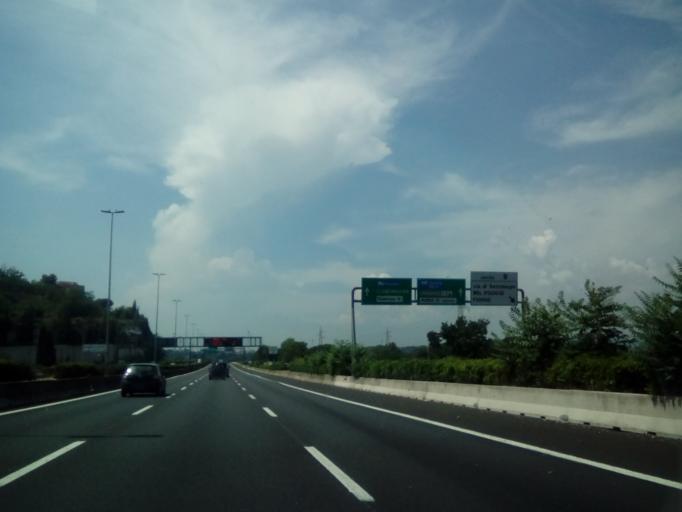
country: IT
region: Latium
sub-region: Citta metropolitana di Roma Capitale
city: Monte Caminetto
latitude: 41.9862
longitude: 12.5196
